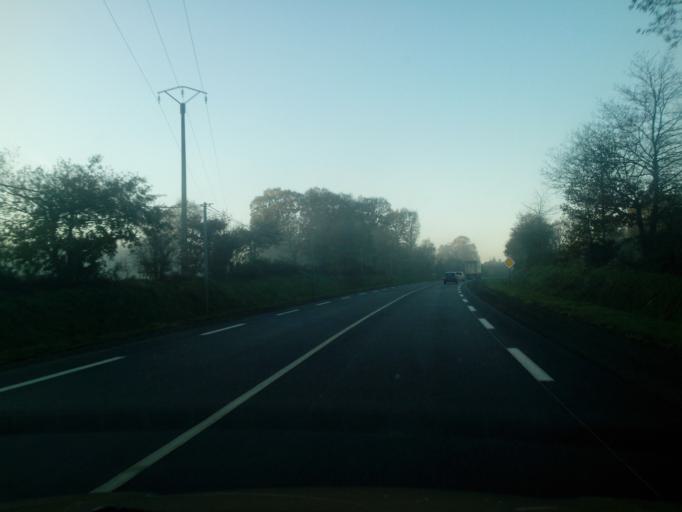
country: FR
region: Brittany
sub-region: Departement du Morbihan
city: Mauron
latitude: 48.0331
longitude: -2.3041
